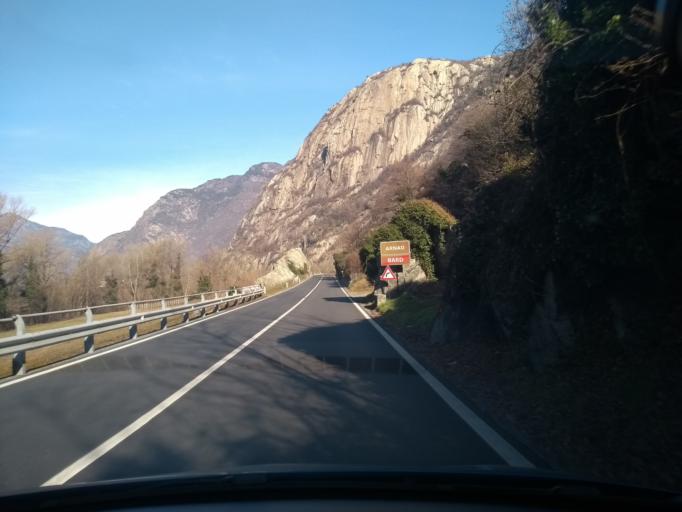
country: IT
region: Aosta Valley
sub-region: Valle d'Aosta
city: Hone
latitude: 45.6249
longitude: 7.7370
